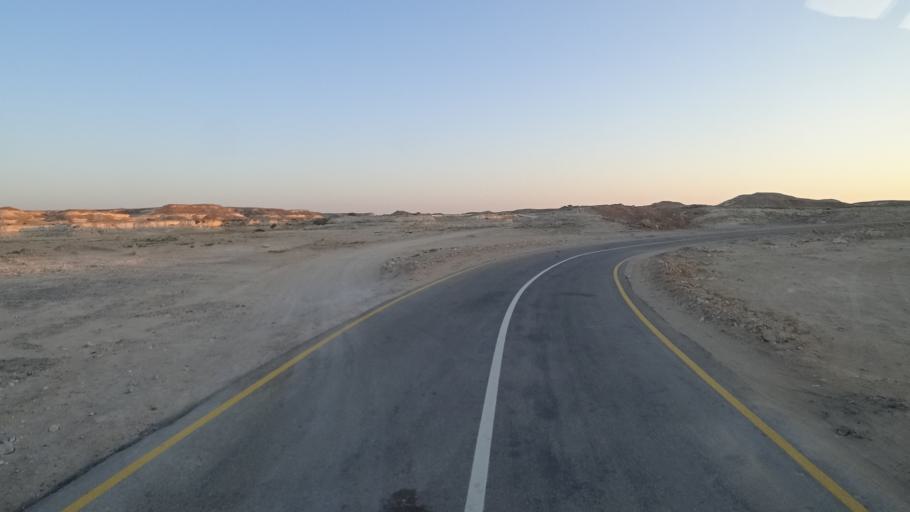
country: OM
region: Zufar
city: Salalah
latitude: 17.4765
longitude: 53.3523
